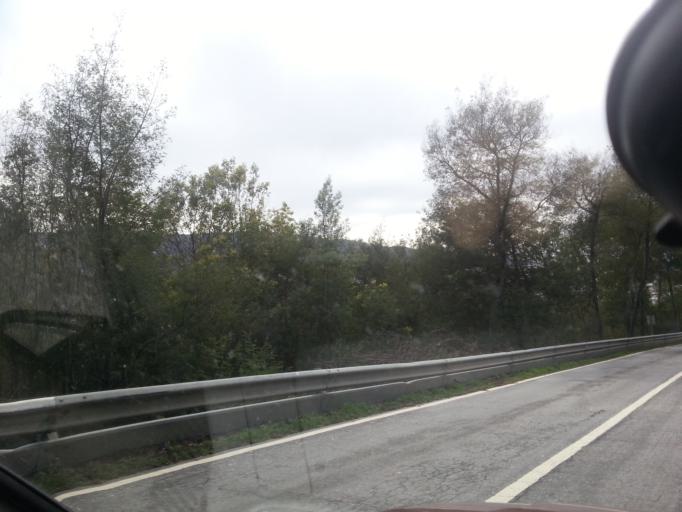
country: PT
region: Guarda
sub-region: Seia
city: Seia
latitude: 40.4378
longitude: -7.7102
